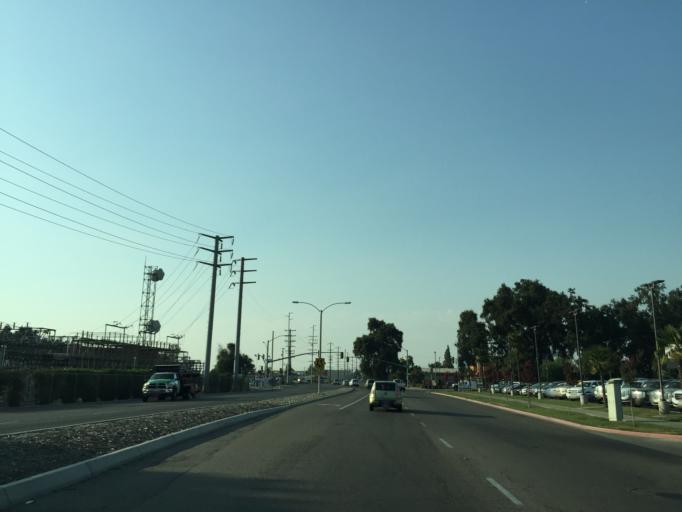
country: US
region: California
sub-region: Tulare County
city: Visalia
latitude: 36.3290
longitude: -119.2785
